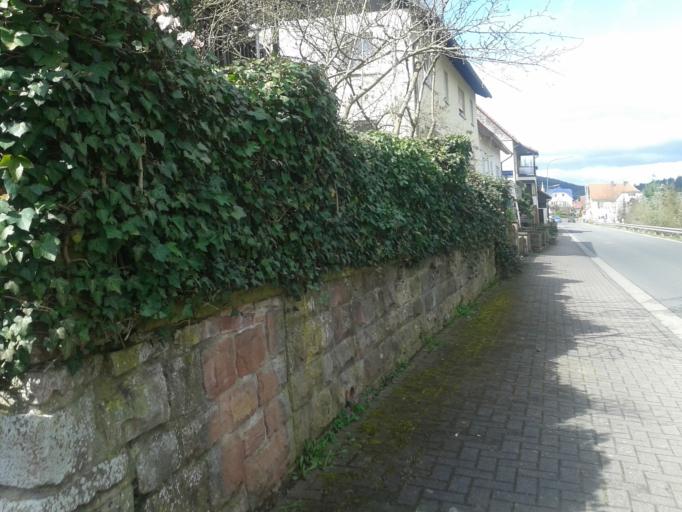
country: DE
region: Bavaria
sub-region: Regierungsbezirk Unterfranken
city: Obersinn
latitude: 50.2366
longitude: 9.5967
